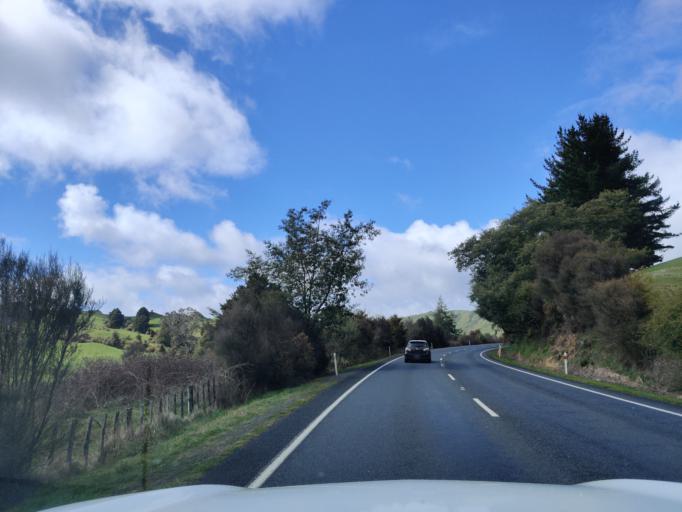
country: NZ
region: Waikato
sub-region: Otorohanga District
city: Otorohanga
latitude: -38.5871
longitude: 175.2166
